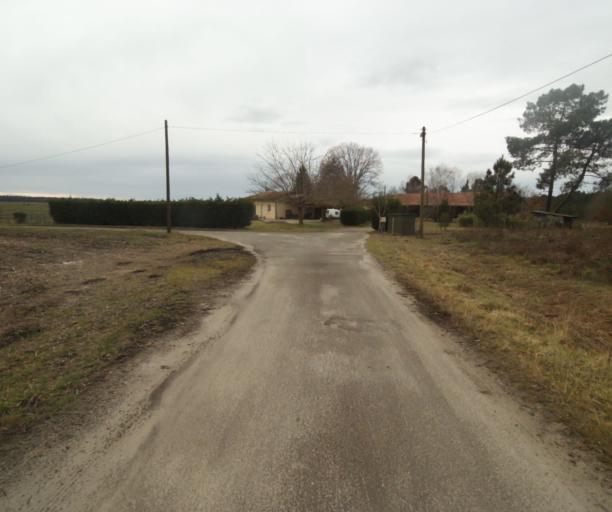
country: FR
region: Aquitaine
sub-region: Departement des Landes
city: Gabarret
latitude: 44.0370
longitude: -0.0761
